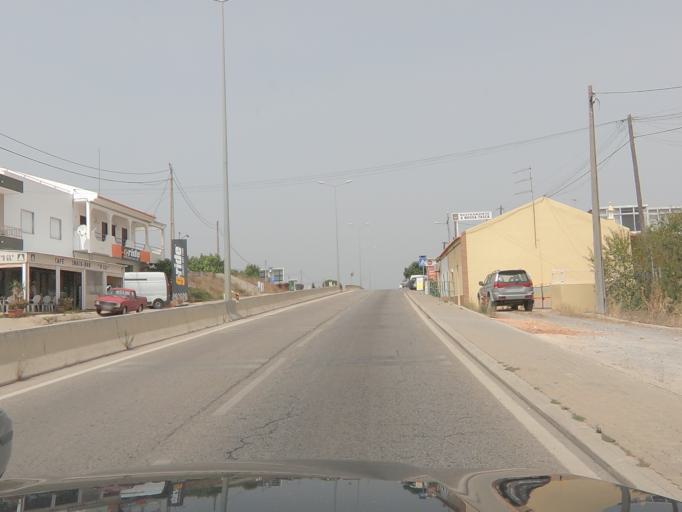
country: PT
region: Faro
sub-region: Portimao
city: Portimao
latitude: 37.1631
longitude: -8.5334
